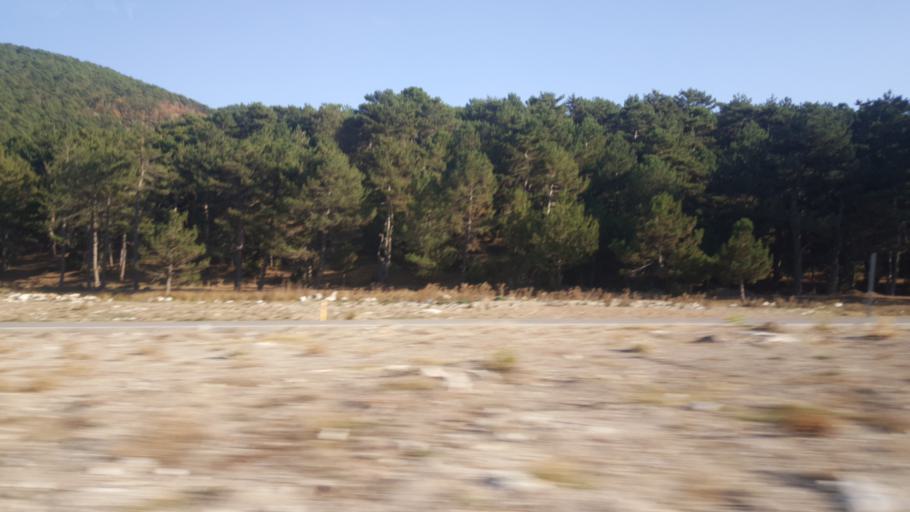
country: TR
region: Afyonkarahisar
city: Ihsaniye
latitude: 39.0992
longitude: 30.5770
